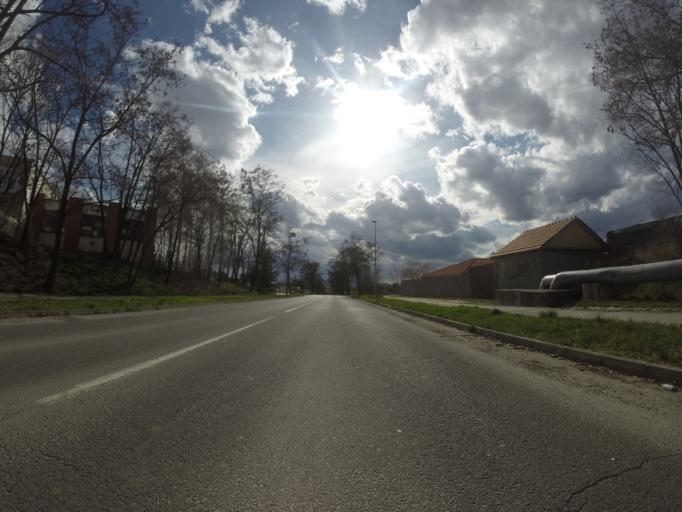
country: SK
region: Nitriansky
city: Prievidza
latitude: 48.7798
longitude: 18.6362
